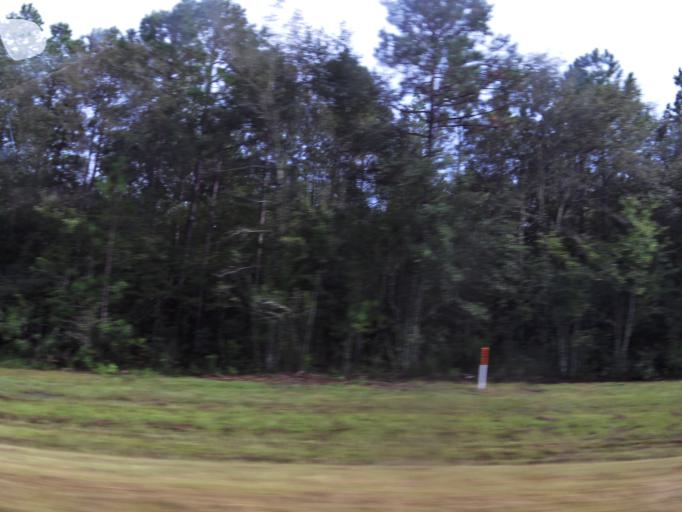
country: US
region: Georgia
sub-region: Long County
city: Ludowici
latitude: 31.7418
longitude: -81.6920
